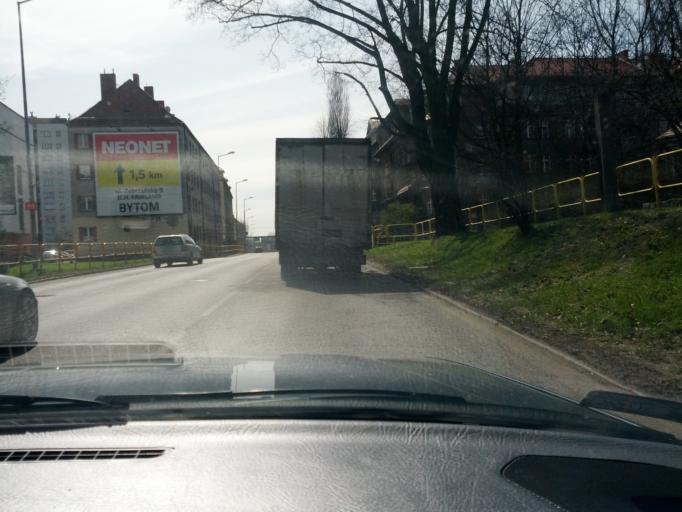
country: PL
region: Silesian Voivodeship
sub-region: Bytom
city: Bytom
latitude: 50.3479
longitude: 18.9143
